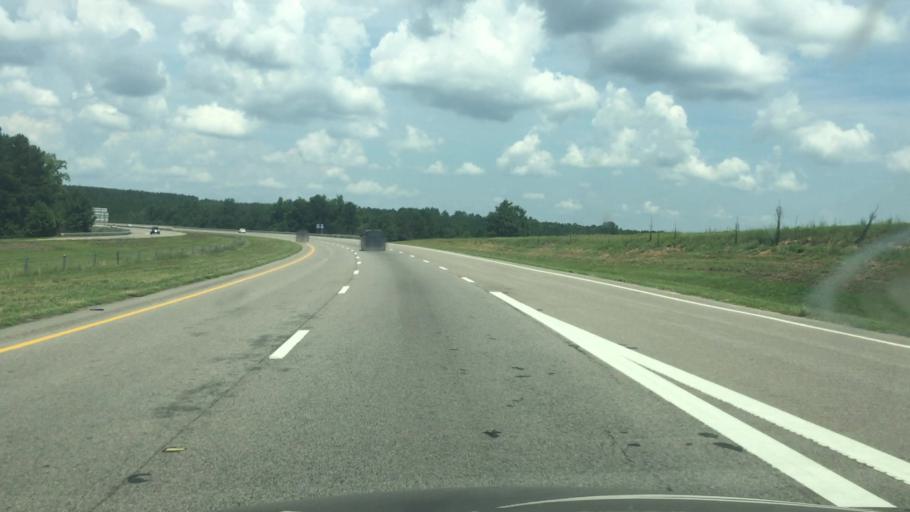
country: US
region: North Carolina
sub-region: Richmond County
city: Ellerbe
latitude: 35.1771
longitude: -79.7128
